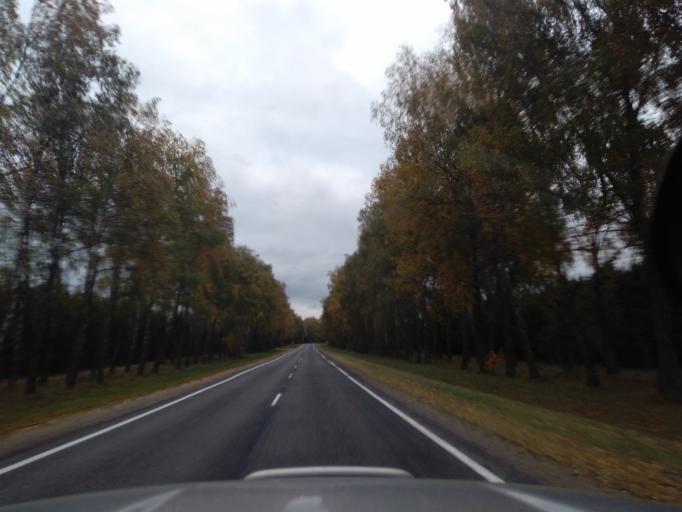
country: BY
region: Minsk
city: Slutsk
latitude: 53.2215
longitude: 27.4901
